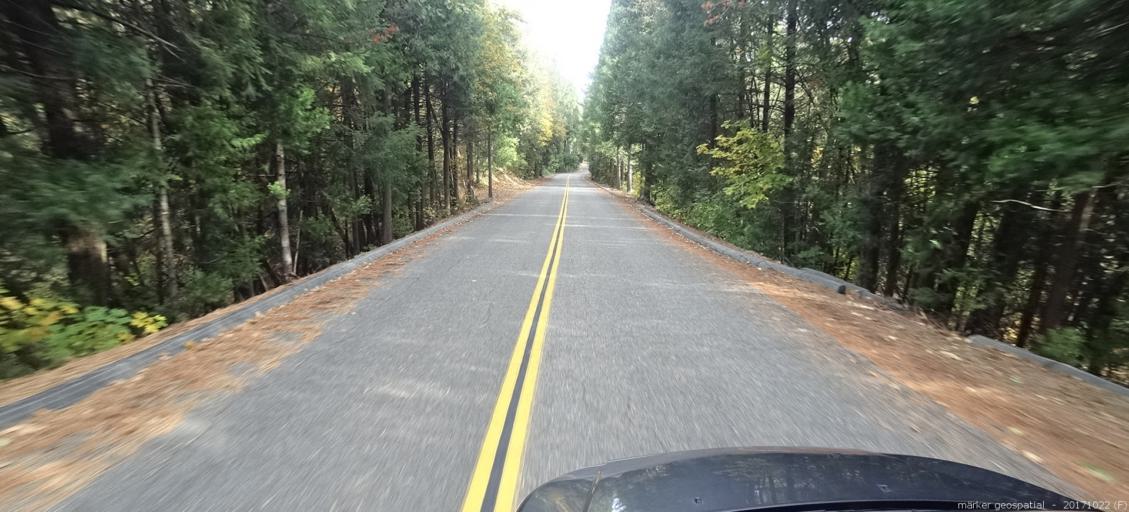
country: US
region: California
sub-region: Siskiyou County
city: Dunsmuir
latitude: 41.1234
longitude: -122.3242
